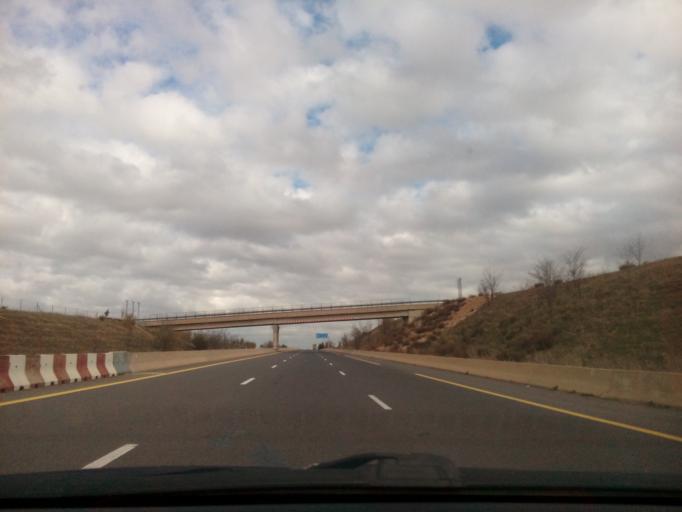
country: DZ
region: Tlemcen
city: Bensekrane
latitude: 34.9970
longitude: -1.1951
